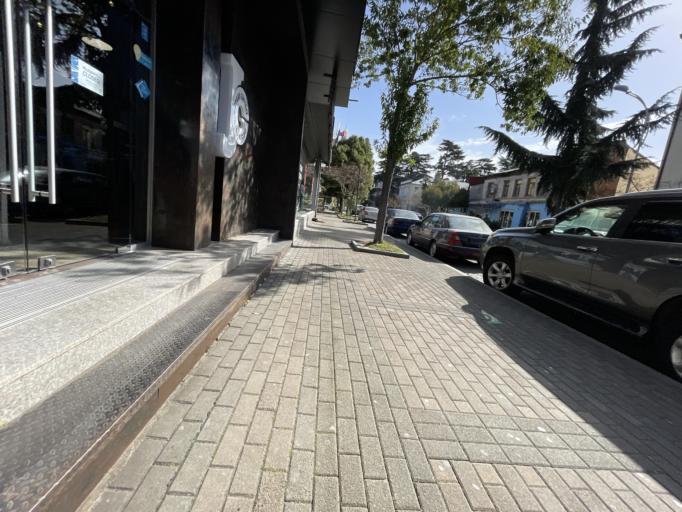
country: GE
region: Ajaria
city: Batumi
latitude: 41.6475
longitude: 41.6374
